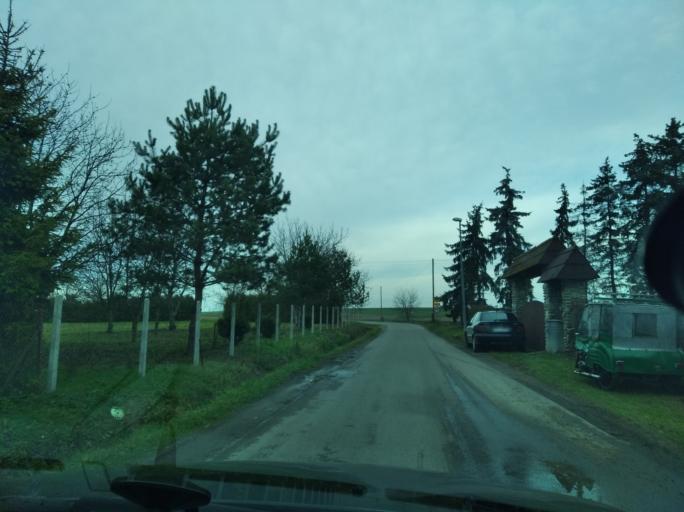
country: PL
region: Subcarpathian Voivodeship
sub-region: Powiat przeworski
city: Przeworsk
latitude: 50.0632
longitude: 22.4730
